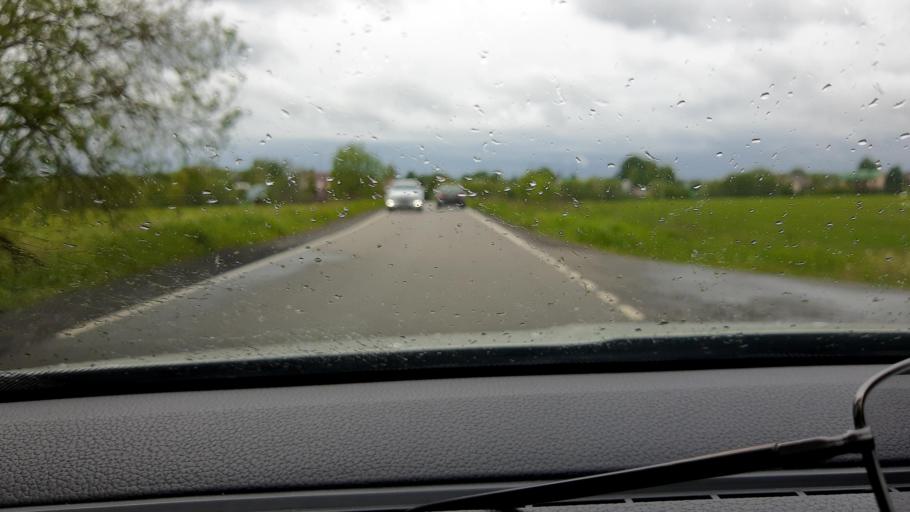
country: RU
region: Moskovskaya
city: Nikolina Gora
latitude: 55.7498
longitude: 36.9803
